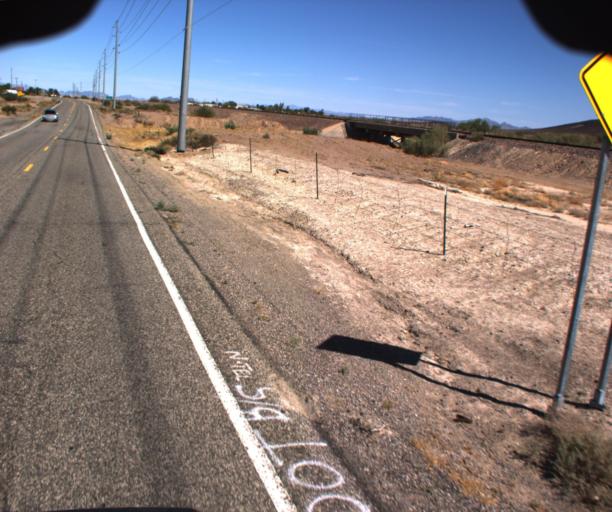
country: US
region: Arizona
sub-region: La Paz County
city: Cienega Springs
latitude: 33.9241
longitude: -113.9992
